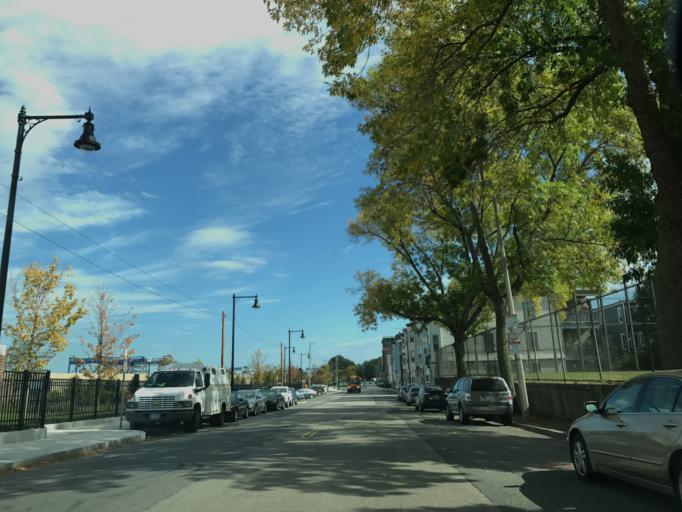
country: US
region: Massachusetts
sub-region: Suffolk County
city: South Boston
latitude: 42.3382
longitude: -71.0313
